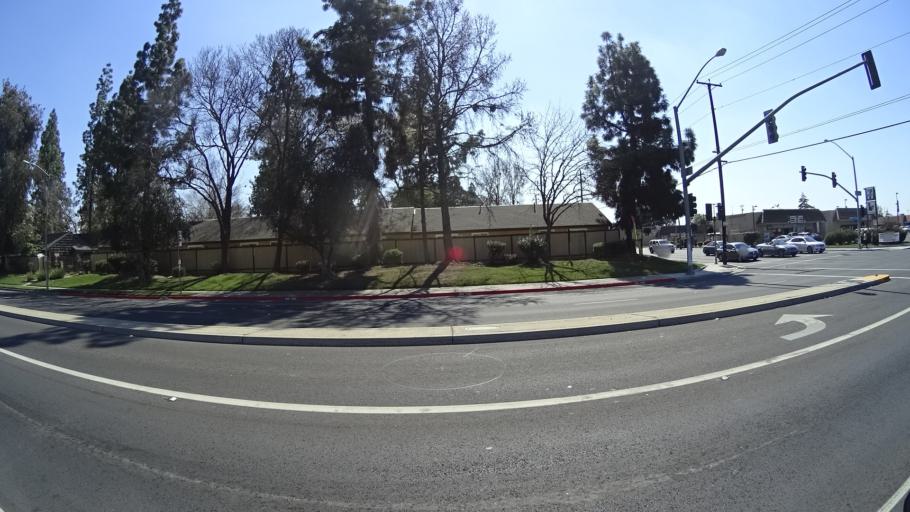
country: US
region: California
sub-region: Fresno County
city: West Park
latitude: 36.7938
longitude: -119.8439
